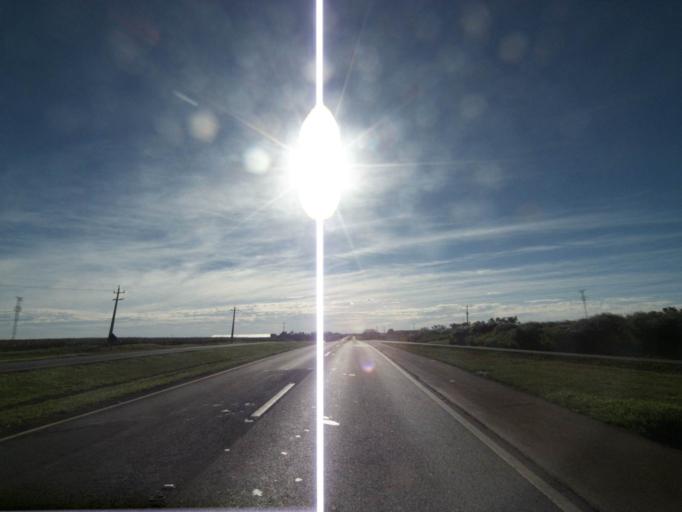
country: BR
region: Parana
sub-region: Cascavel
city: Cascavel
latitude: -25.0224
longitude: -53.5485
